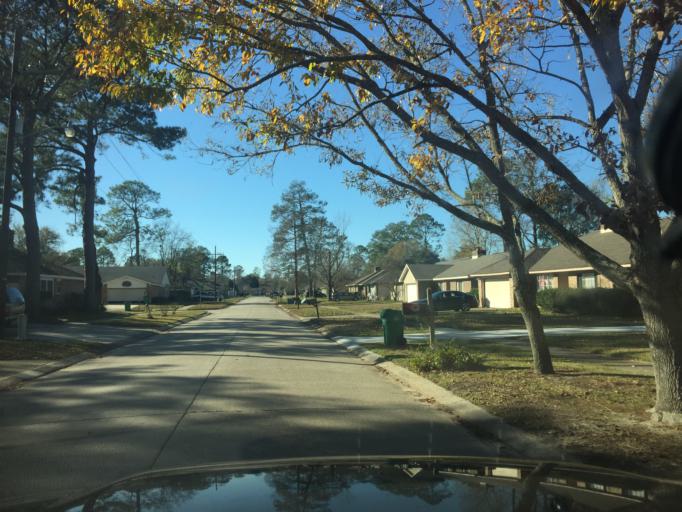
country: US
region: Louisiana
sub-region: Saint Tammany Parish
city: Slidell
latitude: 30.2934
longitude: -89.7515
